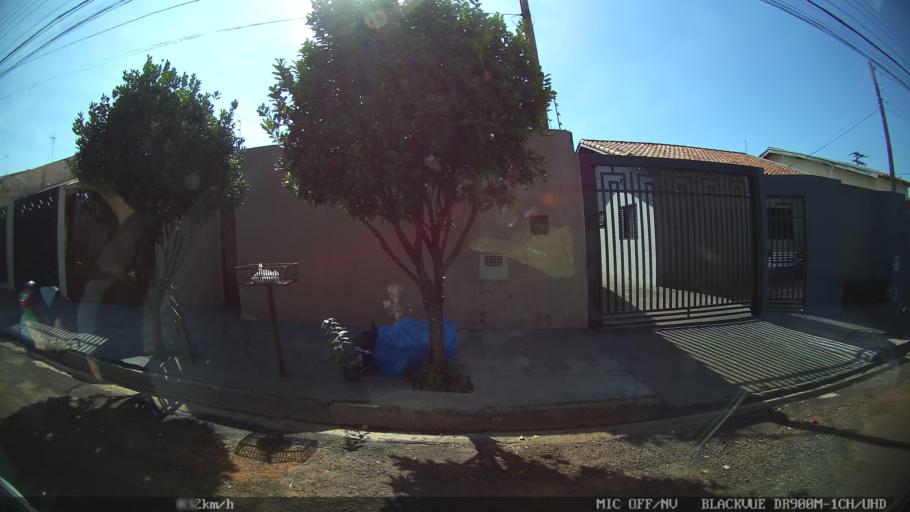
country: BR
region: Sao Paulo
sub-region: Sao Jose Do Rio Preto
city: Sao Jose do Rio Preto
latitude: -20.7887
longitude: -49.4376
